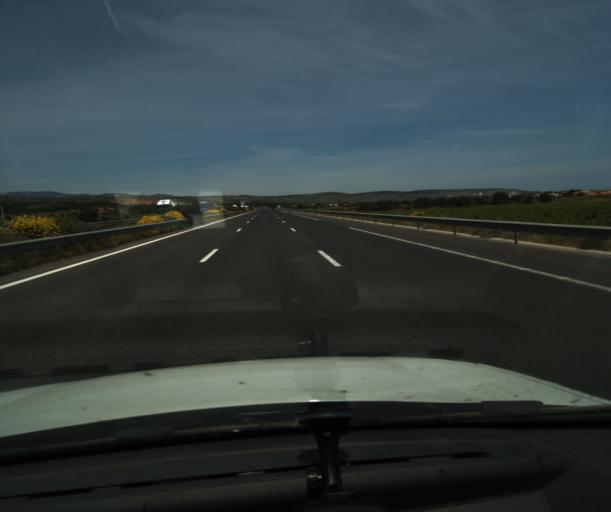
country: FR
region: Languedoc-Roussillon
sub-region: Departement des Pyrenees-Orientales
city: Salses-le-Chateau
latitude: 42.8213
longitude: 2.9087
